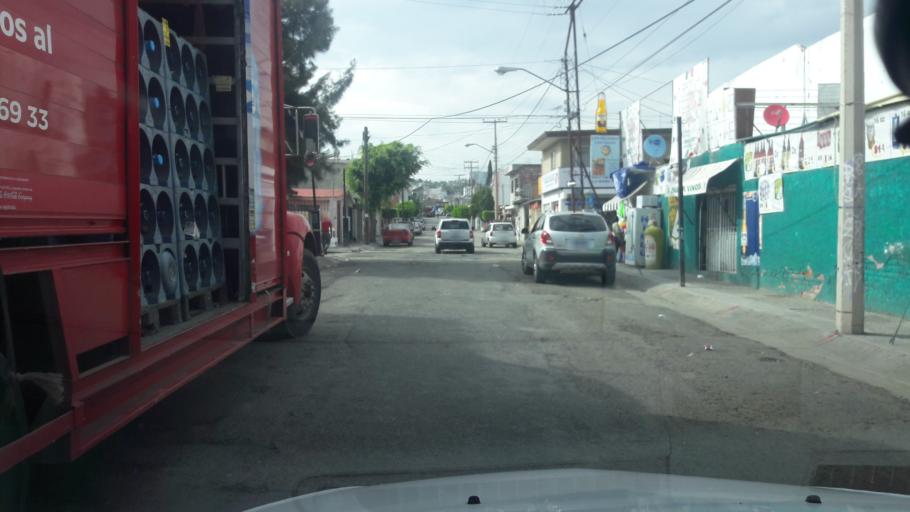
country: MX
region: Guanajuato
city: Leon
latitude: 21.1437
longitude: -101.6990
